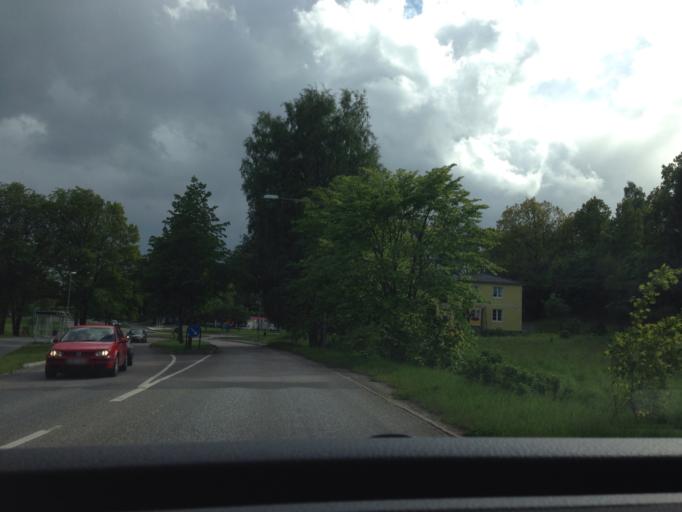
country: SE
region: Vaestra Goetaland
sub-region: Skovde Kommun
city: Skoevde
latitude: 58.4122
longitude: 13.8667
